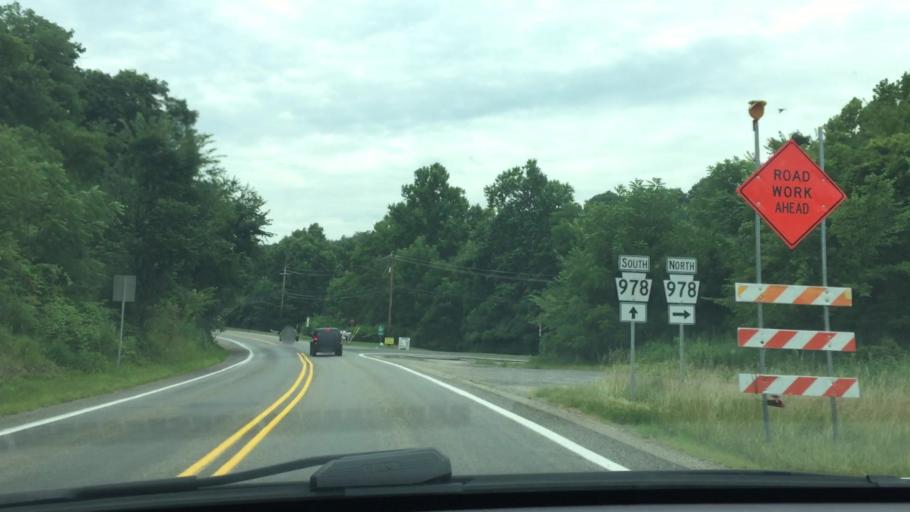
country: US
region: Pennsylvania
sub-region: Allegheny County
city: Oakdale
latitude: 40.4100
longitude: -80.1923
